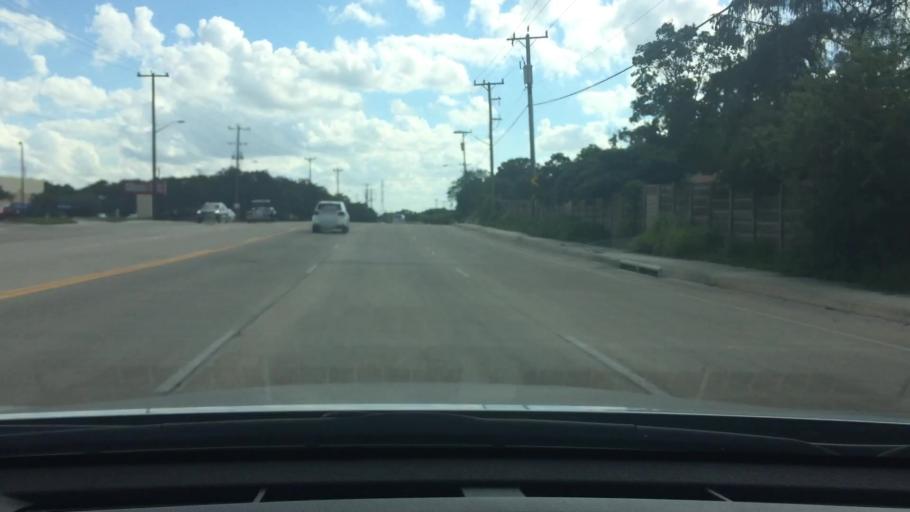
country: US
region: Texas
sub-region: Bexar County
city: Hollywood Park
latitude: 29.6433
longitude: -98.4249
